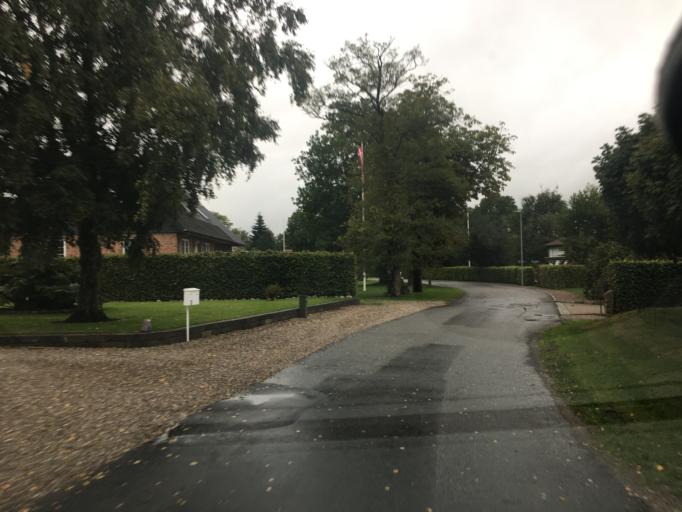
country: DE
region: Schleswig-Holstein
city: Ellhoft
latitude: 54.9378
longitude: 8.9569
